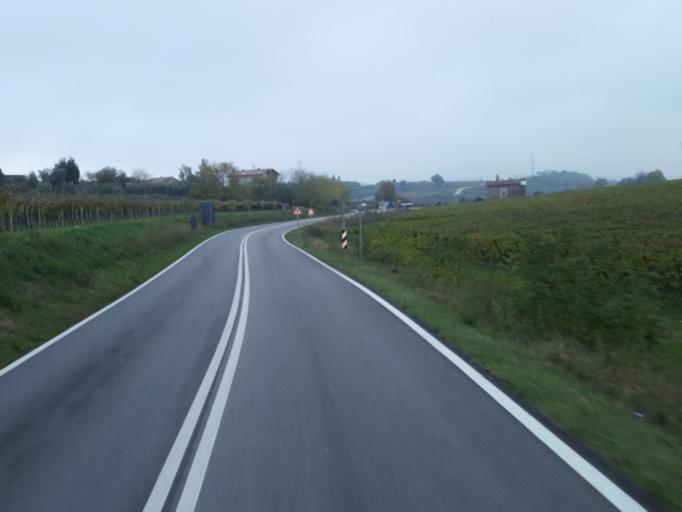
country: IT
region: Veneto
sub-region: Provincia di Verona
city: Calmasino
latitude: 45.5129
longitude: 10.7720
